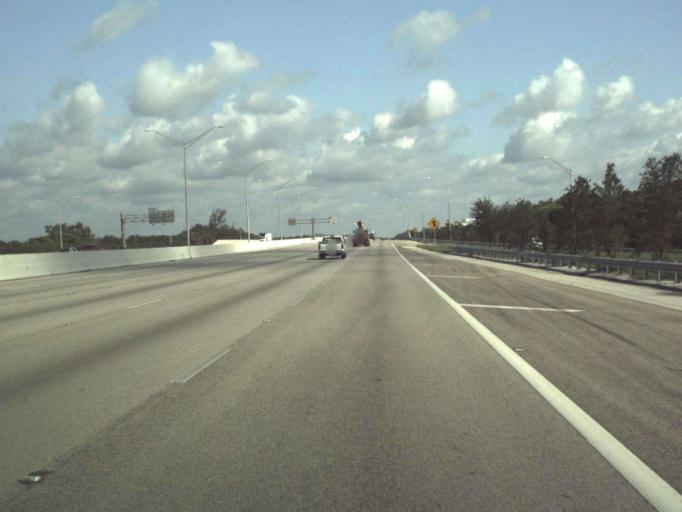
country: US
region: Florida
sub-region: Palm Beach County
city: North Palm Beach
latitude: 26.8412
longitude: -80.1026
